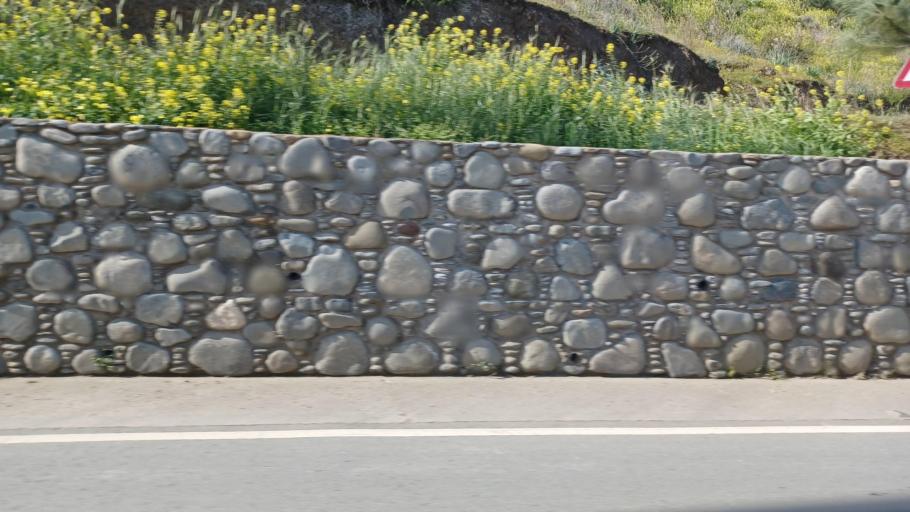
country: CY
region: Lefkosia
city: Lefka
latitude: 35.0828
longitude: 32.8896
